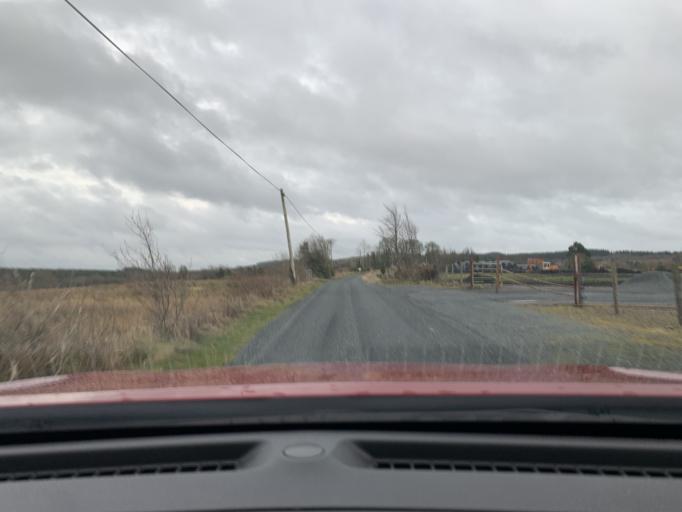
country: IE
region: Connaught
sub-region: Roscommon
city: Ballaghaderreen
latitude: 53.9691
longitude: -8.5208
